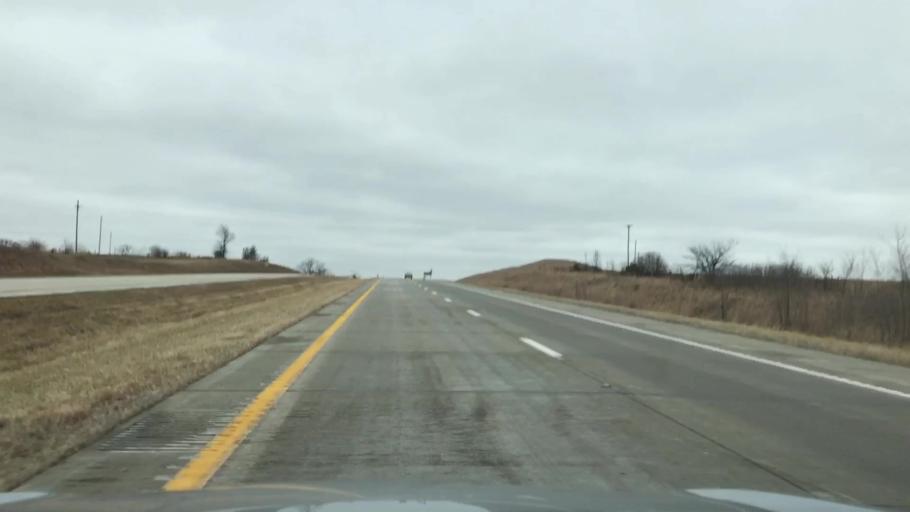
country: US
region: Missouri
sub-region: Caldwell County
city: Hamilton
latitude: 39.7353
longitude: -93.9318
